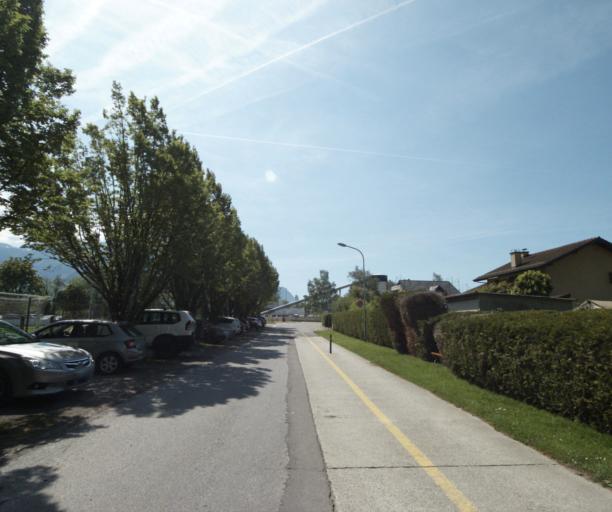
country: CH
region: Vaud
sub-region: Aigle District
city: Villeneuve
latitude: 46.3925
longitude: 6.9247
